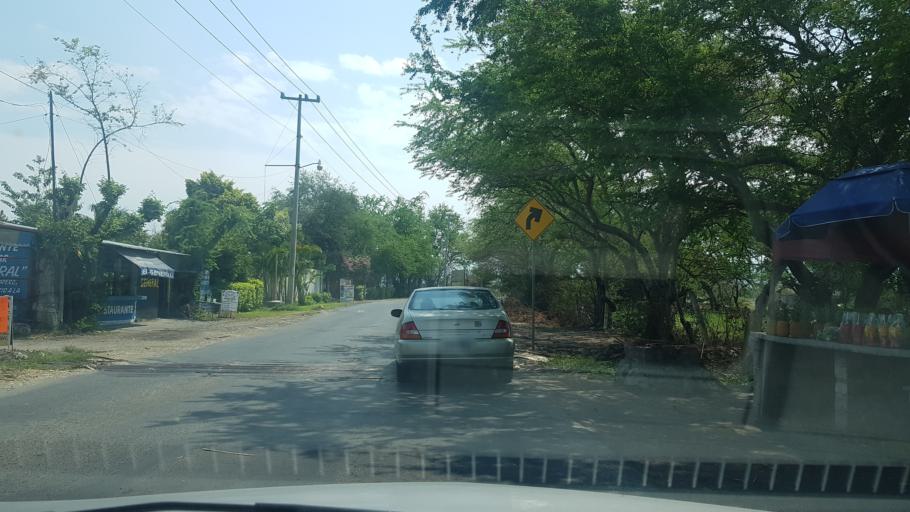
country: MX
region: Morelos
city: Zacatepec
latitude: 18.6597
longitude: -99.1785
